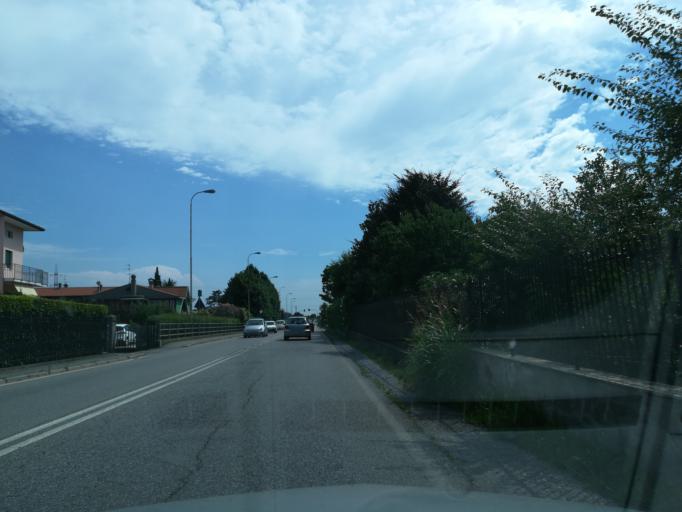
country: IT
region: Lombardy
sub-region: Provincia di Bergamo
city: Almenno San Salvatore
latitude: 45.7459
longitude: 9.6012
